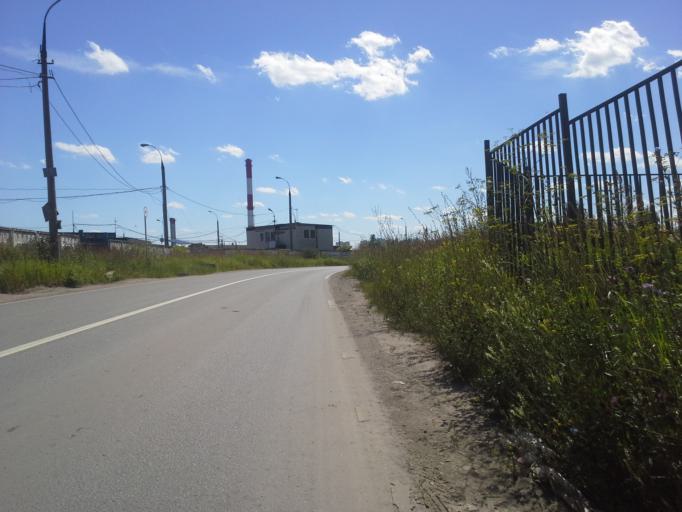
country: RU
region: Moscow
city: Solntsevo
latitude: 55.6602
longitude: 37.3787
